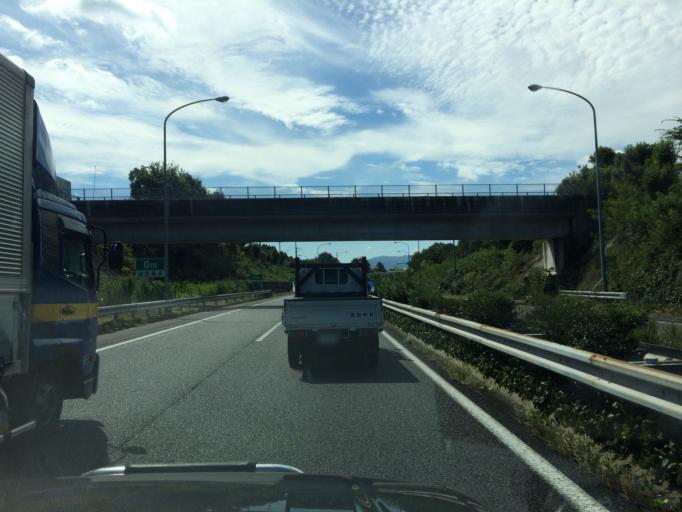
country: JP
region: Osaka
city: Izumi
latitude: 34.4849
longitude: 135.4654
